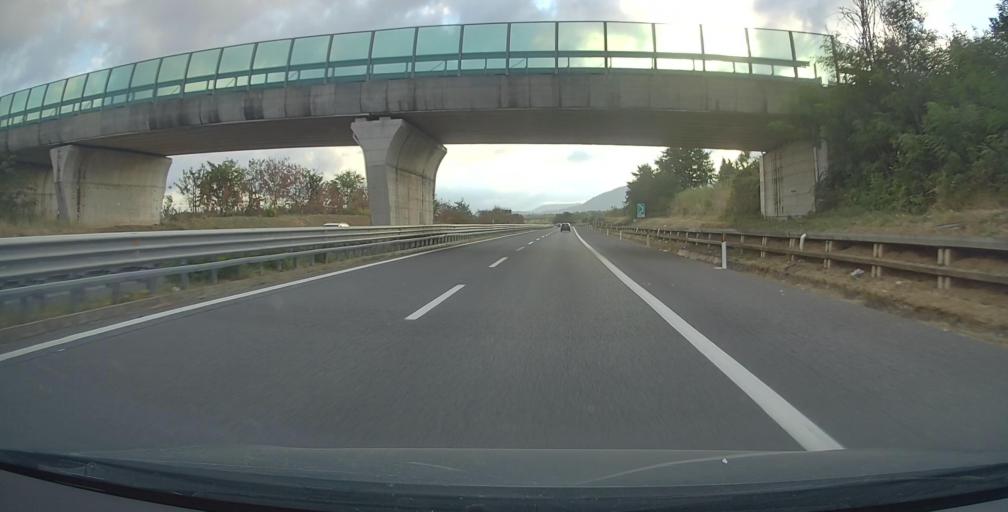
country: IT
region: Calabria
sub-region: Provincia di Catanzaro
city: Acconia
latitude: 38.8215
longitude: 16.2433
